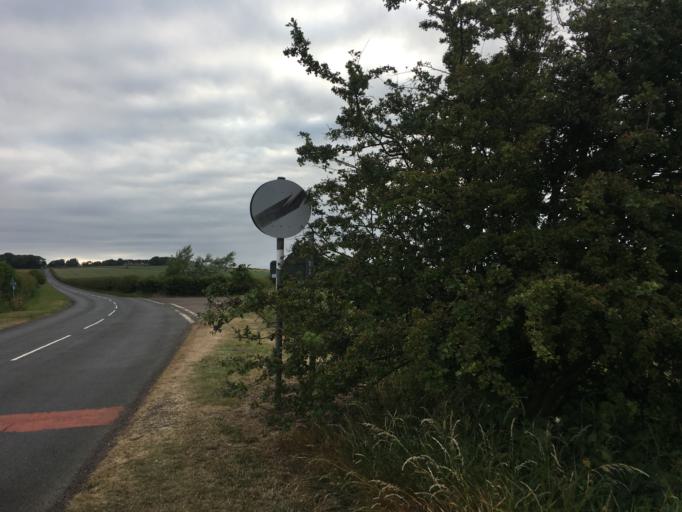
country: GB
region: England
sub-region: Northumberland
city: Lowick
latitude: 55.6549
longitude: -1.9001
